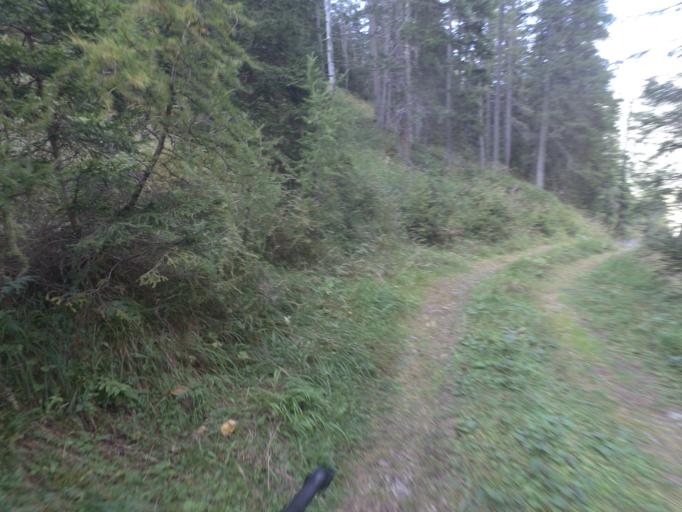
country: AT
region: Salzburg
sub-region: Politischer Bezirk Sankt Johann im Pongau
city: Untertauern
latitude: 47.2403
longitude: 13.4182
